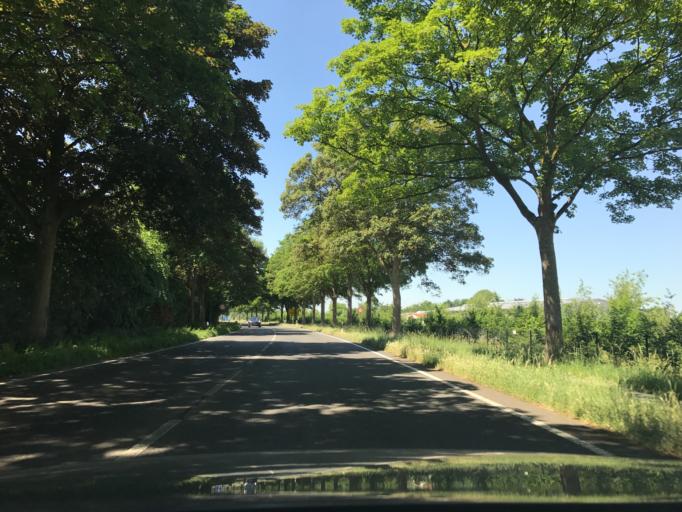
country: DE
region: North Rhine-Westphalia
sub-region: Regierungsbezirk Dusseldorf
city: Wachtendonk
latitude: 51.4125
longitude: 6.3392
